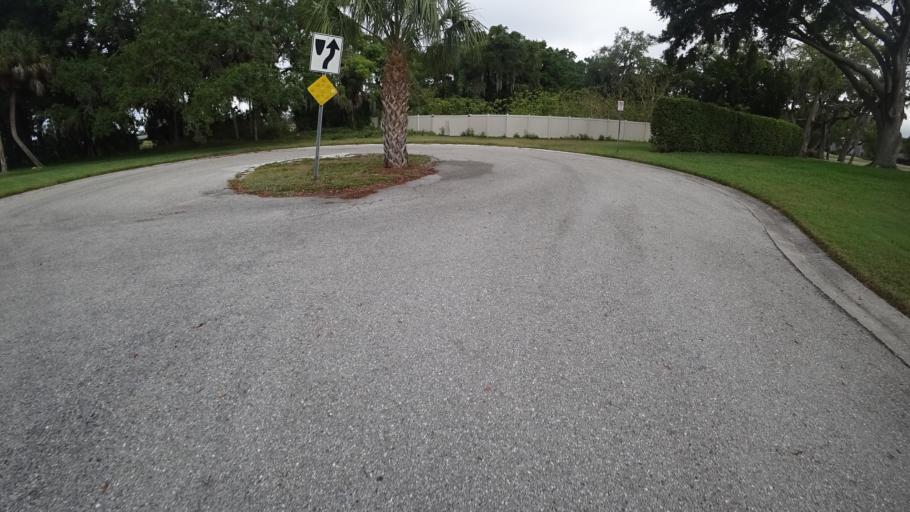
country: US
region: Florida
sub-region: Manatee County
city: Bayshore Gardens
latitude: 27.4327
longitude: -82.6038
